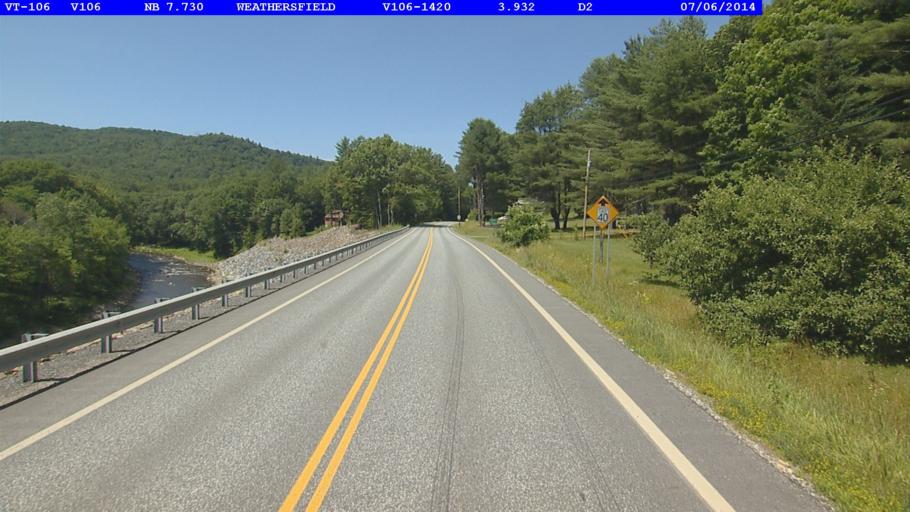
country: US
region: Vermont
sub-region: Windsor County
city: Springfield
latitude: 43.3951
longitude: -72.5140
